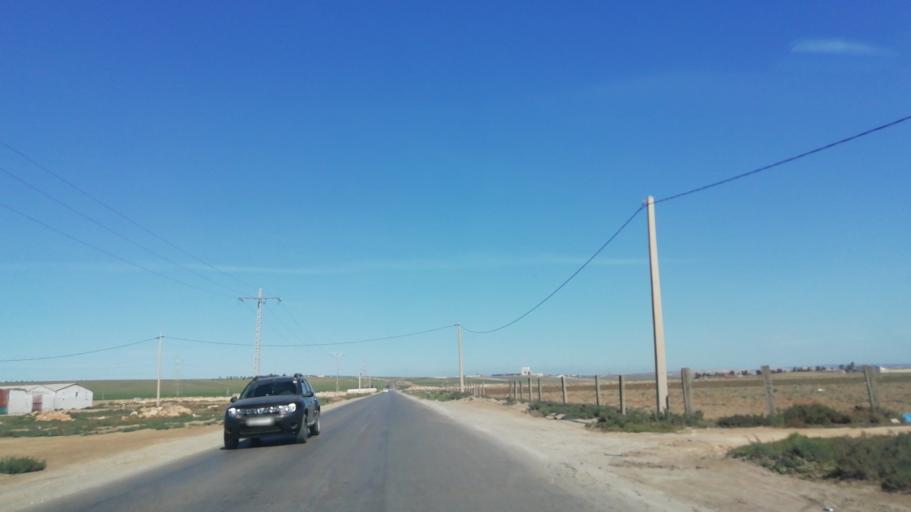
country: DZ
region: Oran
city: Es Senia
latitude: 35.5233
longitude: -0.5876
